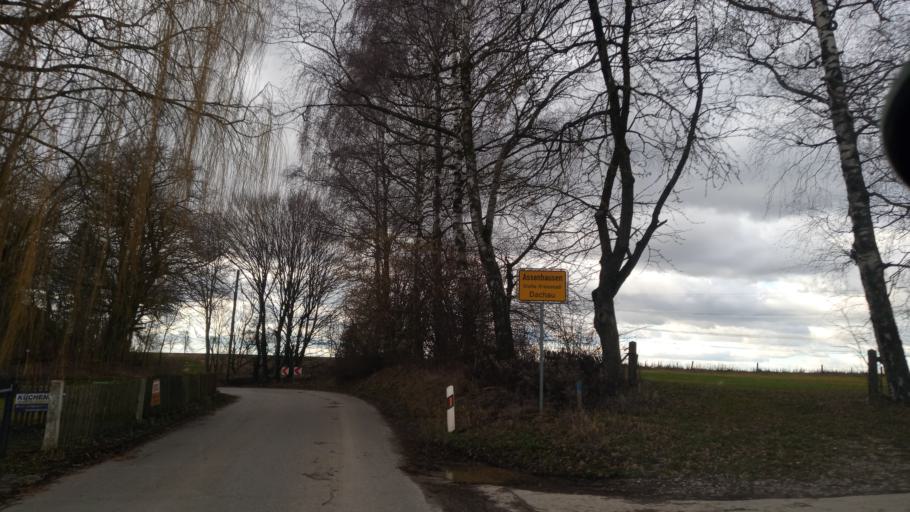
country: DE
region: Bavaria
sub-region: Upper Bavaria
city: Schwabhausen
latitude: 48.3000
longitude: 11.4018
